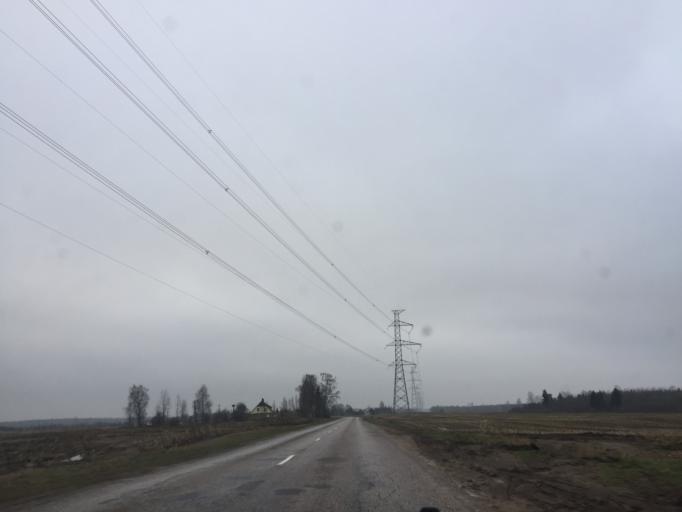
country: LV
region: Limbazu Rajons
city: Limbazi
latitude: 57.5742
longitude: 24.6632
